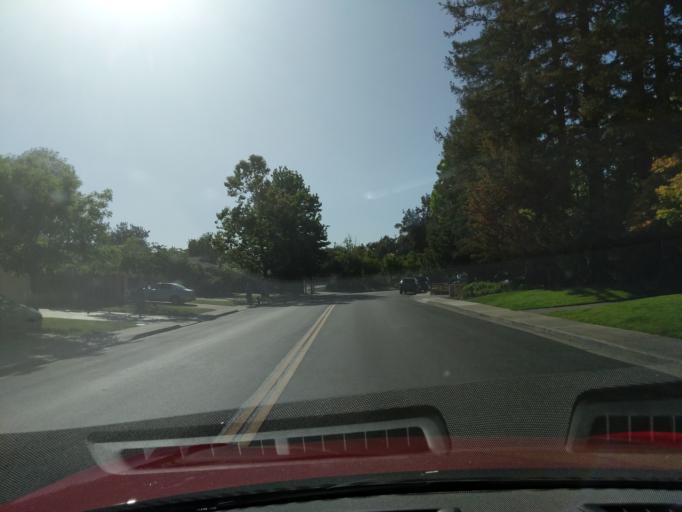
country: US
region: California
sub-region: San Mateo County
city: West Menlo Park
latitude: 37.4272
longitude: -122.1998
